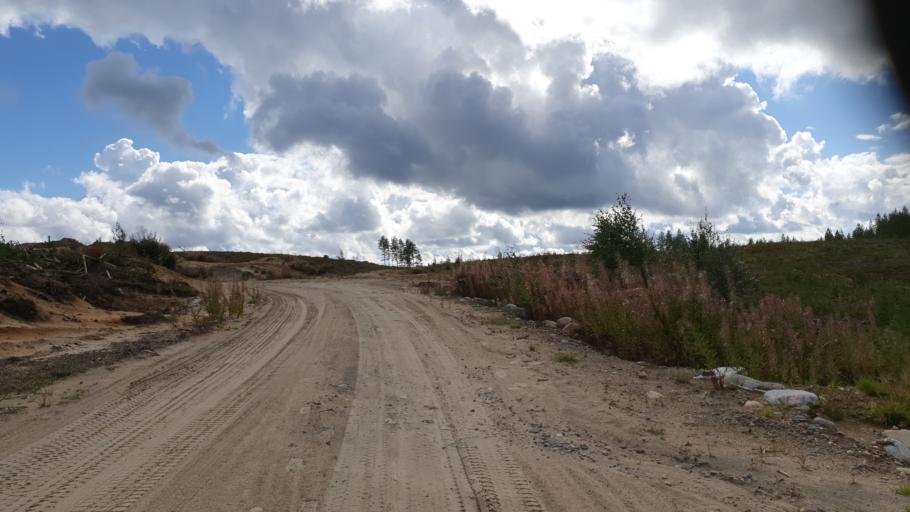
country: FI
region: Kainuu
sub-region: Kehys-Kainuu
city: Kuhmo
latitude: 64.1507
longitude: 29.3693
